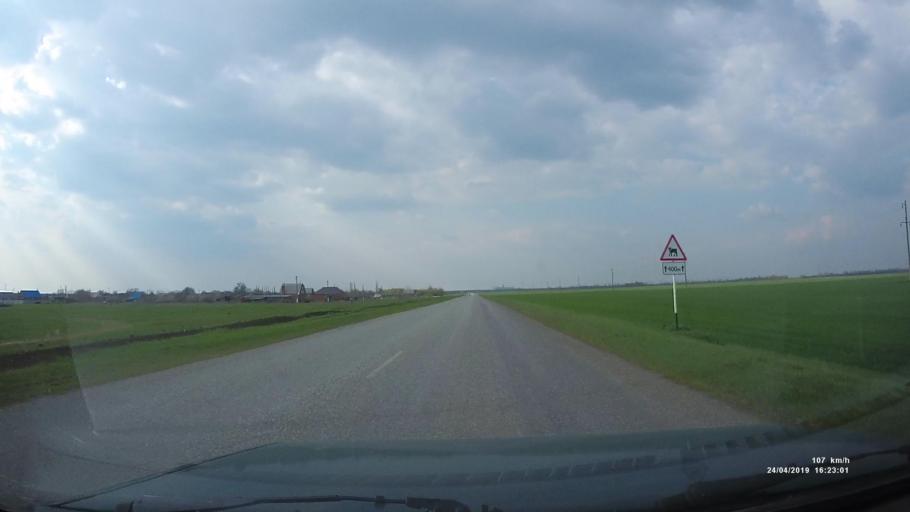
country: RU
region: Rostov
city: Orlovskiy
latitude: 46.8281
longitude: 42.0521
